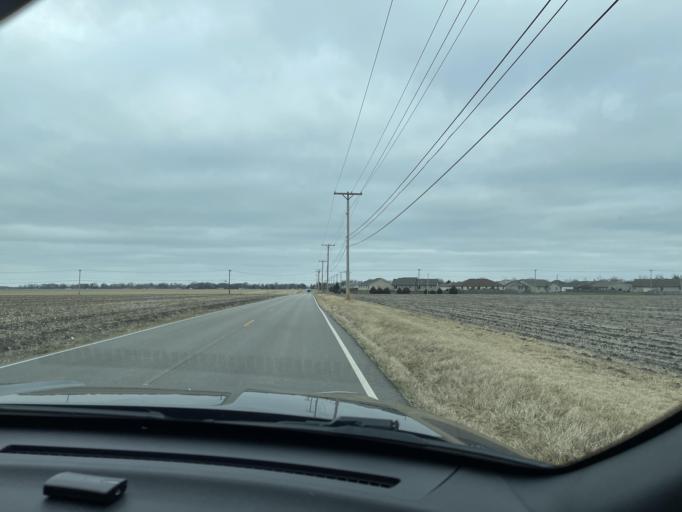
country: US
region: Illinois
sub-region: Sangamon County
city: Jerome
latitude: 39.7688
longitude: -89.7532
